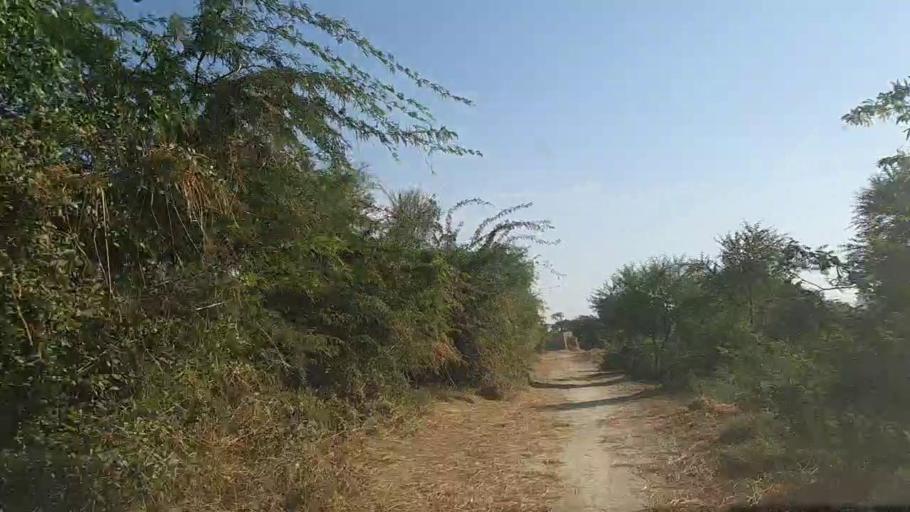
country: PK
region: Sindh
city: Bulri
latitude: 24.8581
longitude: 68.2883
